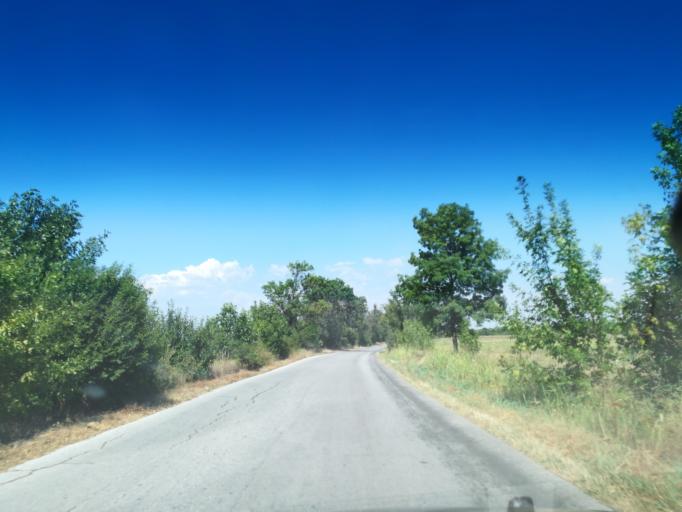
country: BG
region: Stara Zagora
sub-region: Obshtina Chirpan
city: Chirpan
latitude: 42.0632
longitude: 25.1677
